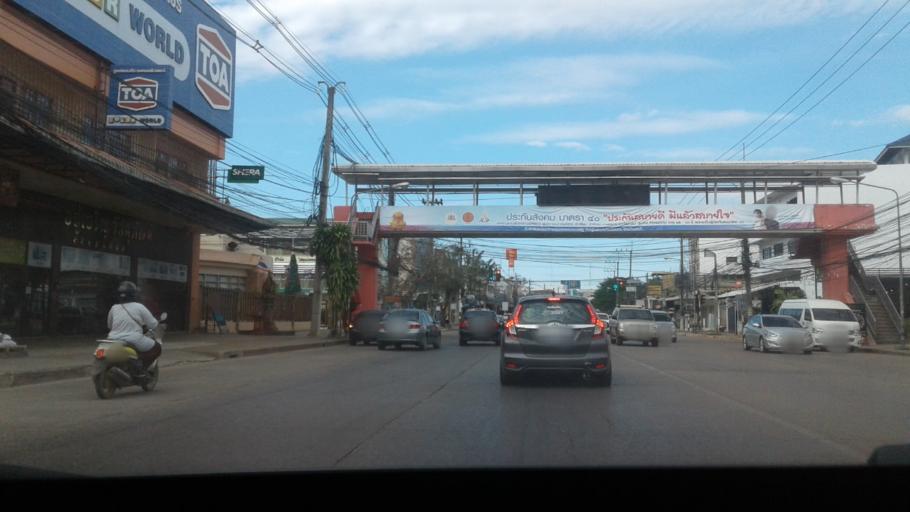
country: TH
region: Changwat Udon Thani
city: Udon Thani
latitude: 17.4227
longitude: 102.7908
